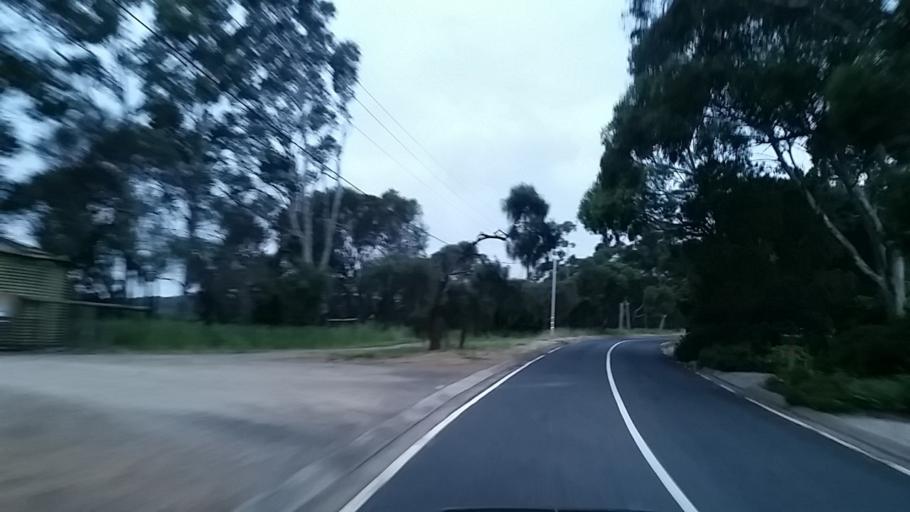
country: AU
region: South Australia
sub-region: Burnside
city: Beaumont
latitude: -34.9499
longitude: 138.6877
